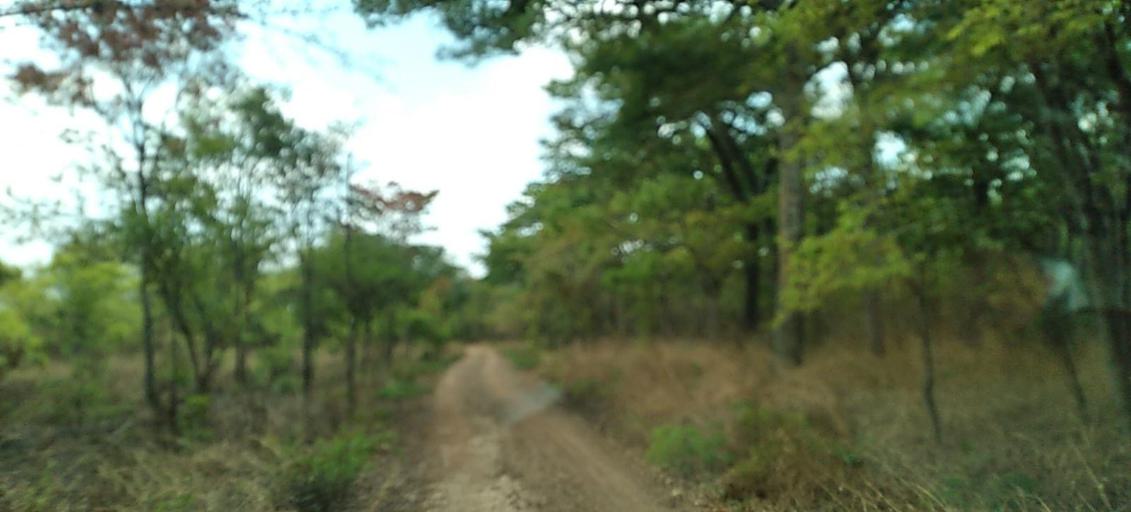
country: ZM
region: Copperbelt
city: Chililabombwe
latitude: -12.4716
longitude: 27.6511
